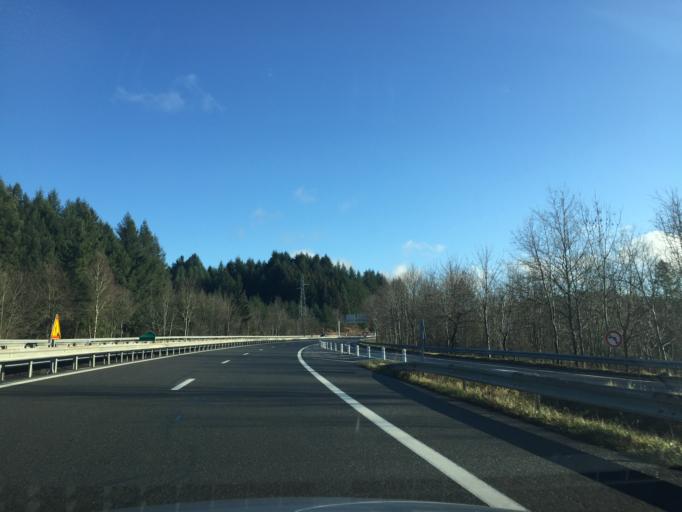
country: FR
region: Auvergne
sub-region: Departement du Puy-de-Dome
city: Celles-sur-Durolle
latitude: 45.8815
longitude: 3.6256
